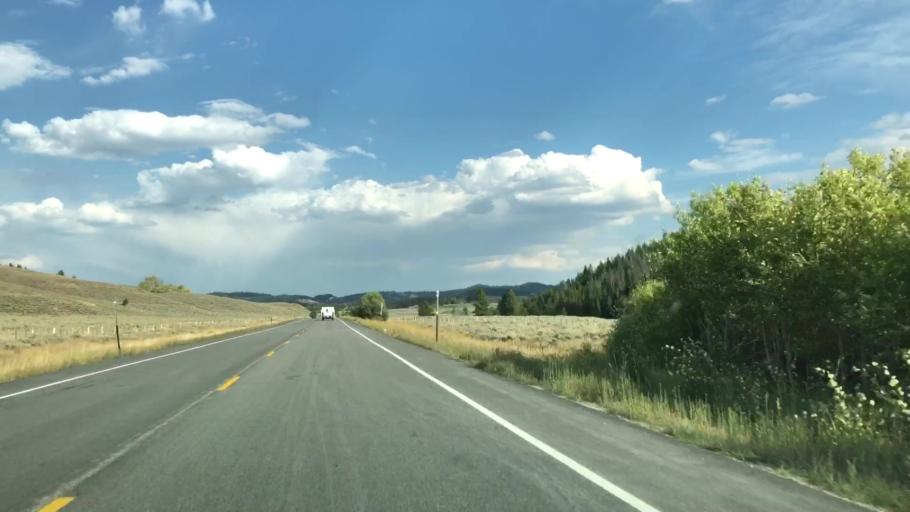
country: US
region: Wyoming
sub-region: Sublette County
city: Pinedale
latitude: 43.1519
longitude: -110.2812
